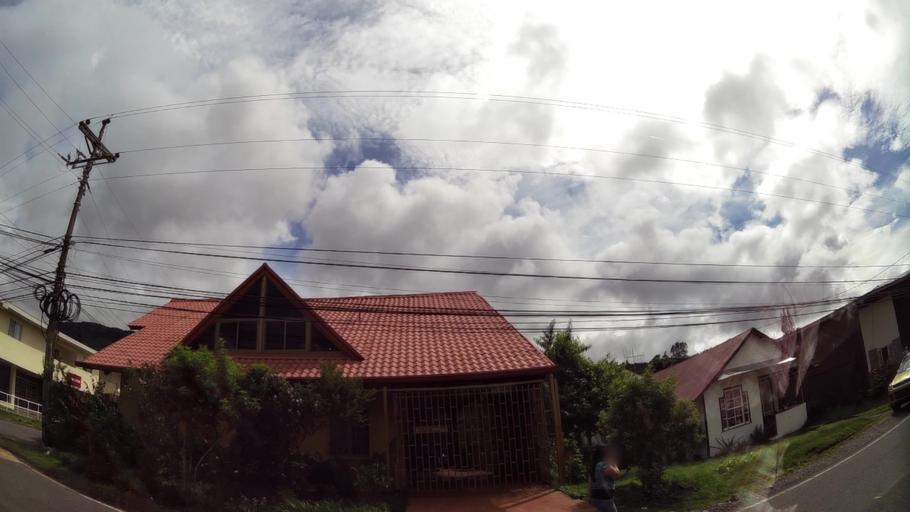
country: PA
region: Chiriqui
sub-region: Distrito Boquete
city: Boquete
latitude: 8.7767
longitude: -82.4336
